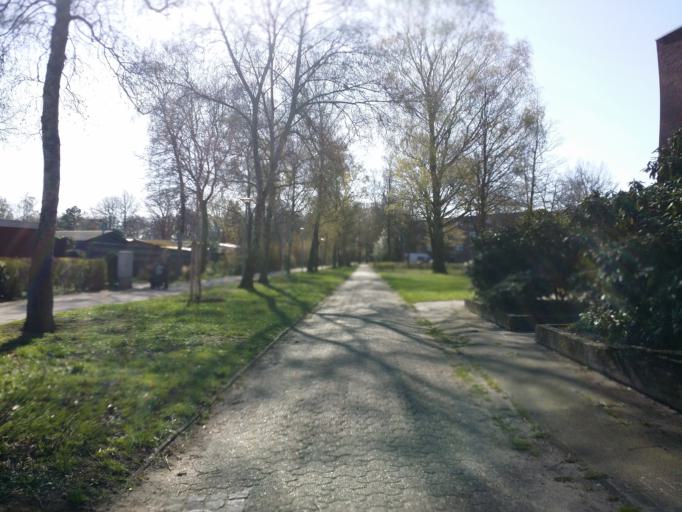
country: DE
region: Lower Saxony
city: Delmenhorst
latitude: 53.0276
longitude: 8.6588
